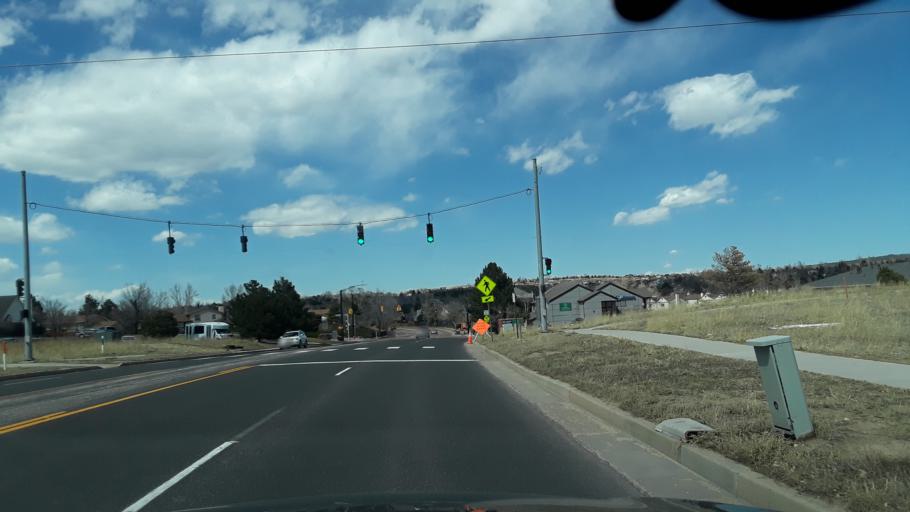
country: US
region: Colorado
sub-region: El Paso County
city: Black Forest
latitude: 38.9403
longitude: -104.7630
